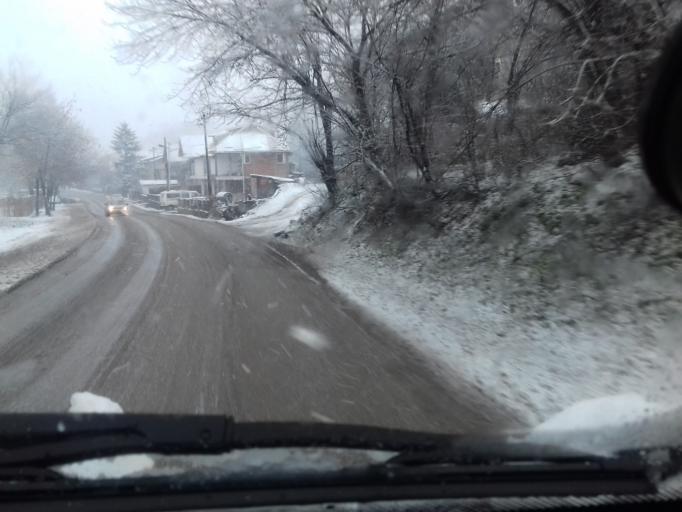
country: BA
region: Federation of Bosnia and Herzegovina
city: Zenica
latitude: 44.1873
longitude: 17.9207
